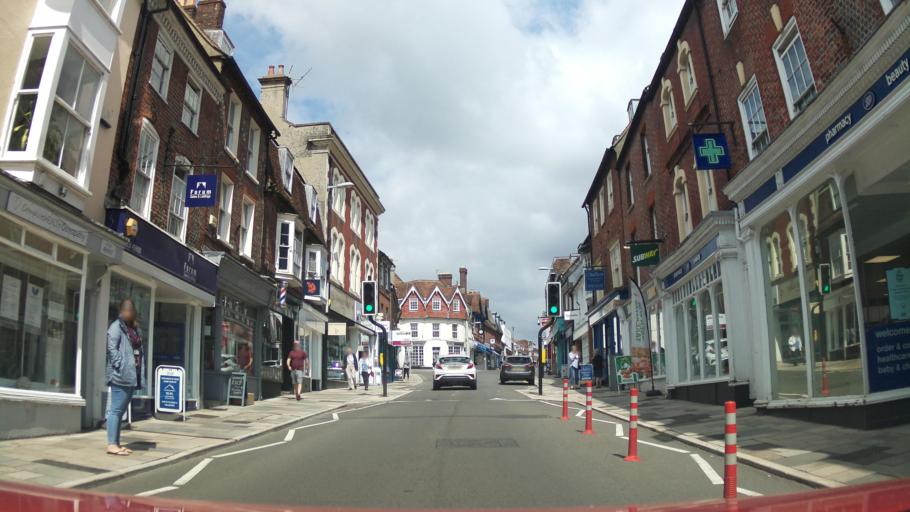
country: GB
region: England
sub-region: Dorset
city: Blandford Forum
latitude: 50.8564
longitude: -2.1654
